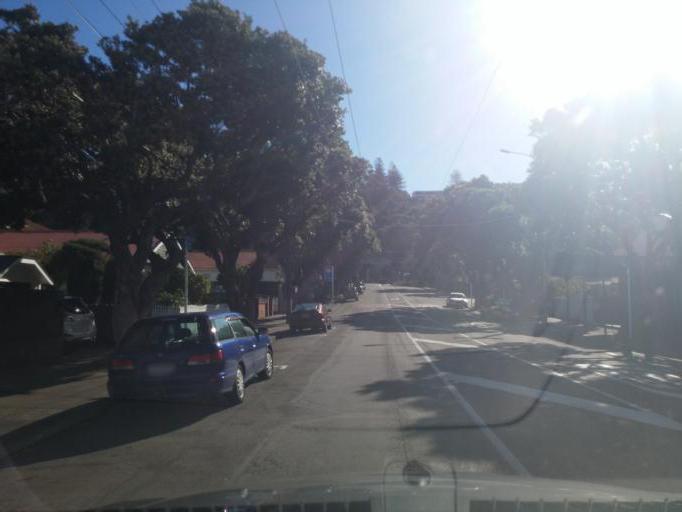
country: NZ
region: Wellington
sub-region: Wellington City
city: Wellington
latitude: -41.3226
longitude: 174.8307
